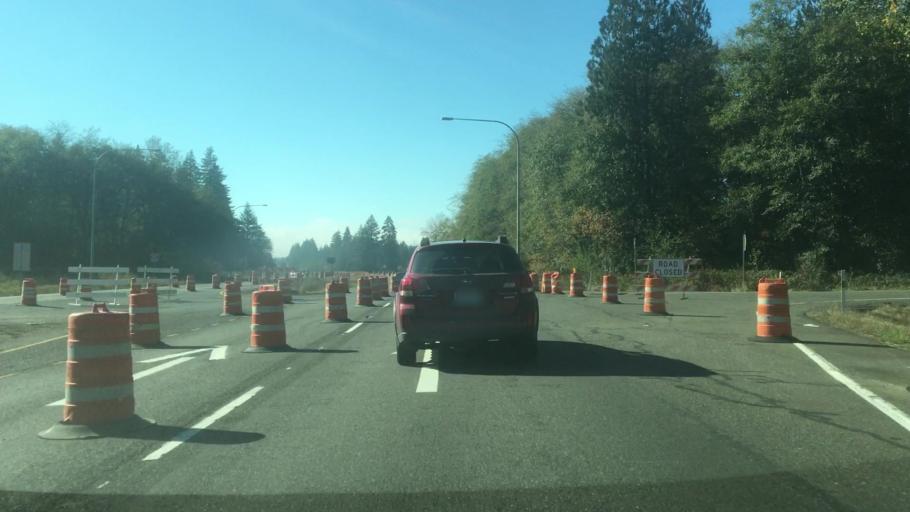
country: US
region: Washington
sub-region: Grays Harbor County
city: McCleary
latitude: 47.0544
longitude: -123.2861
